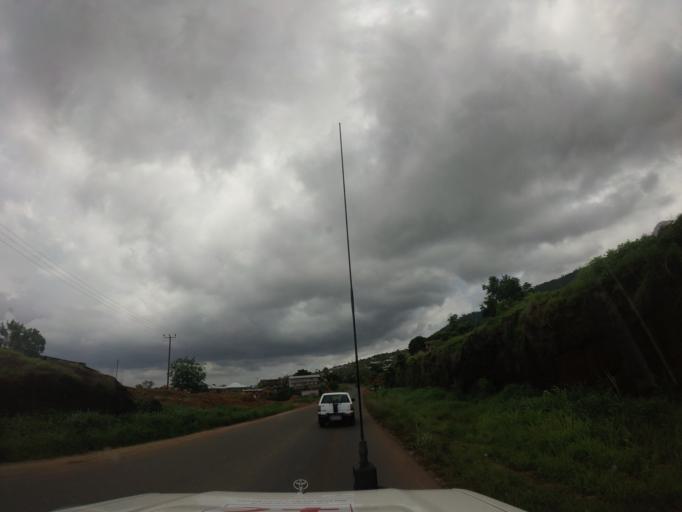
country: SL
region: Western Area
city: Waterloo
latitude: 8.3614
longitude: -13.0833
